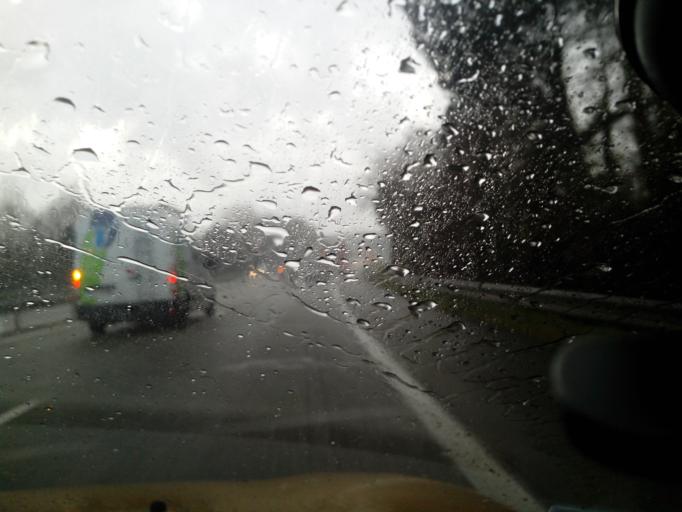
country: FR
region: Brittany
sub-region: Departement du Morbihan
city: Baud
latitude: 47.8716
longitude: -3.0568
